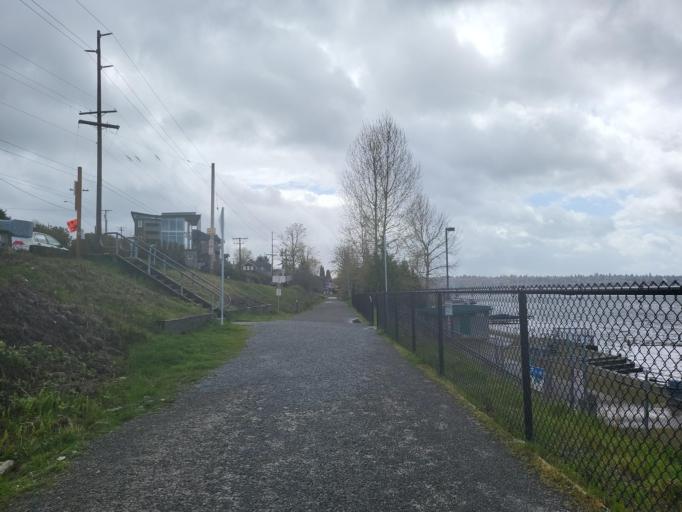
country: US
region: Washington
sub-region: King County
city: Renton
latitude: 47.5236
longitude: -122.2072
